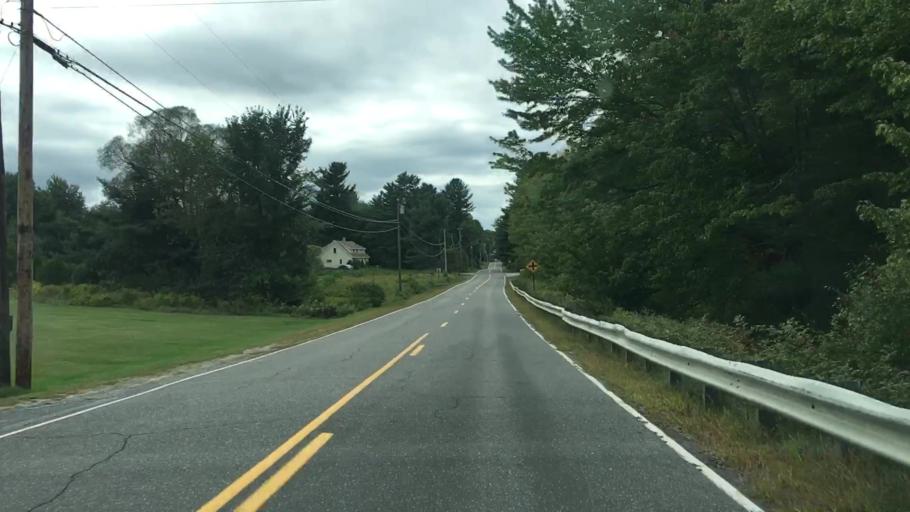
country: US
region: Maine
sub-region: Kennebec County
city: Hallowell
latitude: 44.2761
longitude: -69.8085
